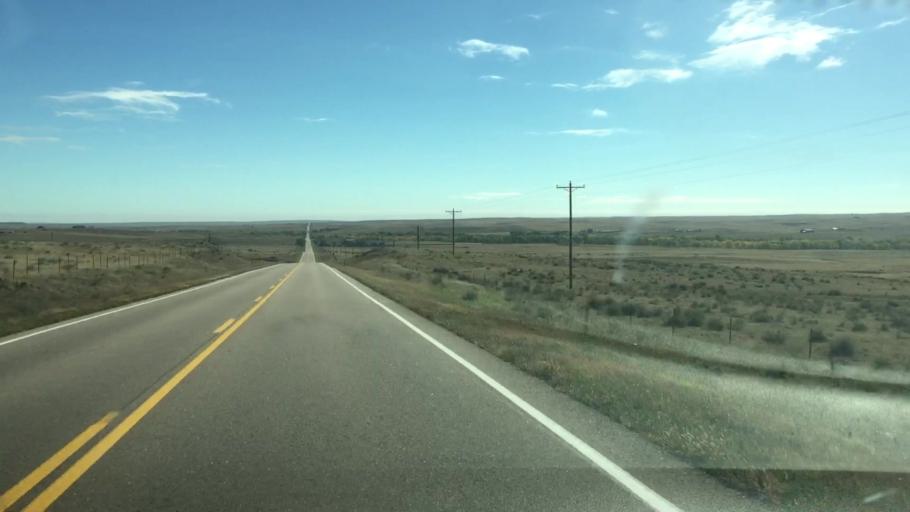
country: US
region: Colorado
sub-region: Elbert County
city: Kiowa
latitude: 39.2735
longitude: -104.1736
